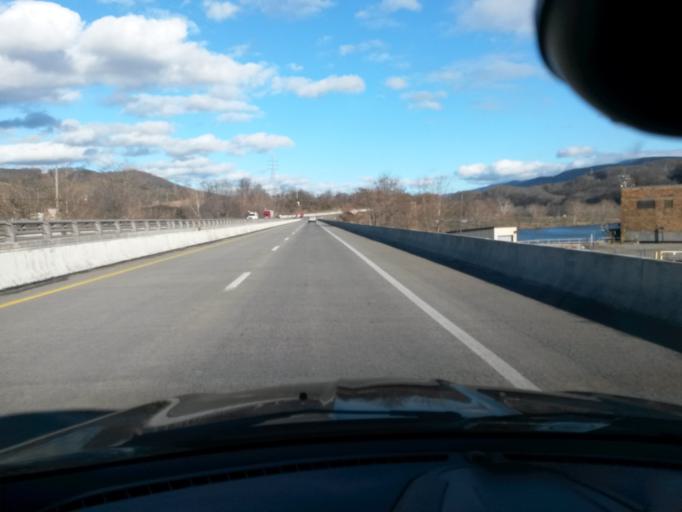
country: US
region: Virginia
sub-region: Giles County
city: Narrows
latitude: 37.3717
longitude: -80.8645
